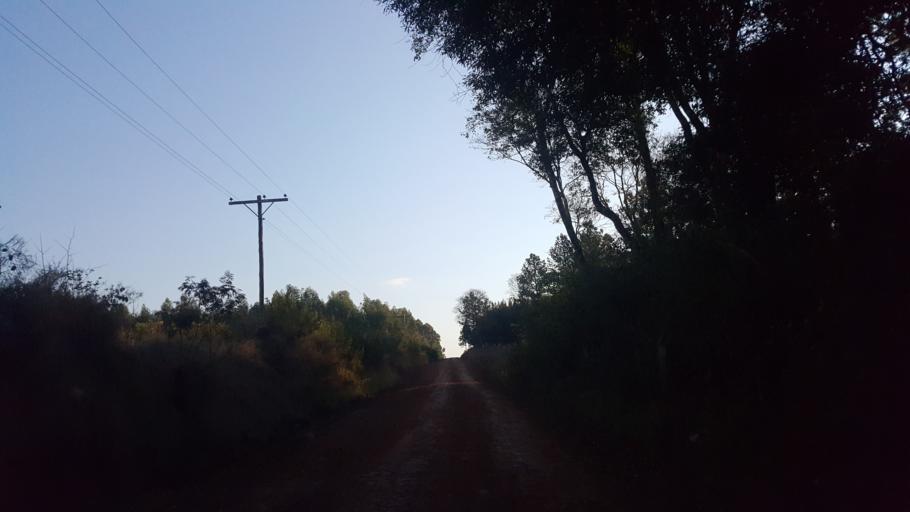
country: AR
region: Misiones
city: Capiovi
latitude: -26.9191
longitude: -55.0518
